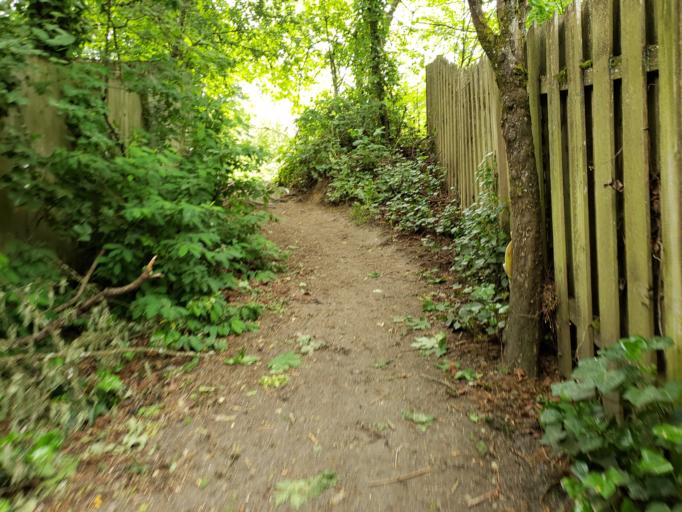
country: US
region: Oregon
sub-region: Washington County
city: Raleigh Hills
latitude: 45.4812
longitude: -122.7328
